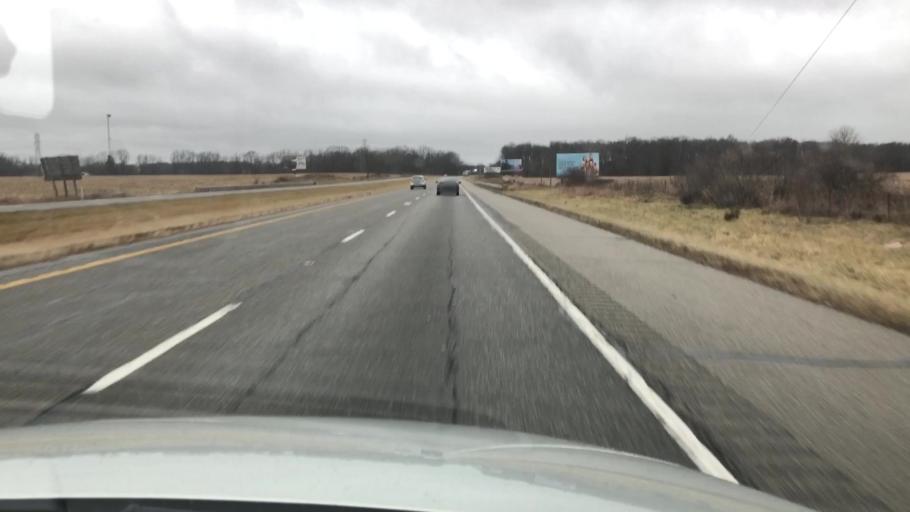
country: US
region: Indiana
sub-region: Marshall County
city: Plymouth
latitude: 41.3615
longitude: -86.3582
